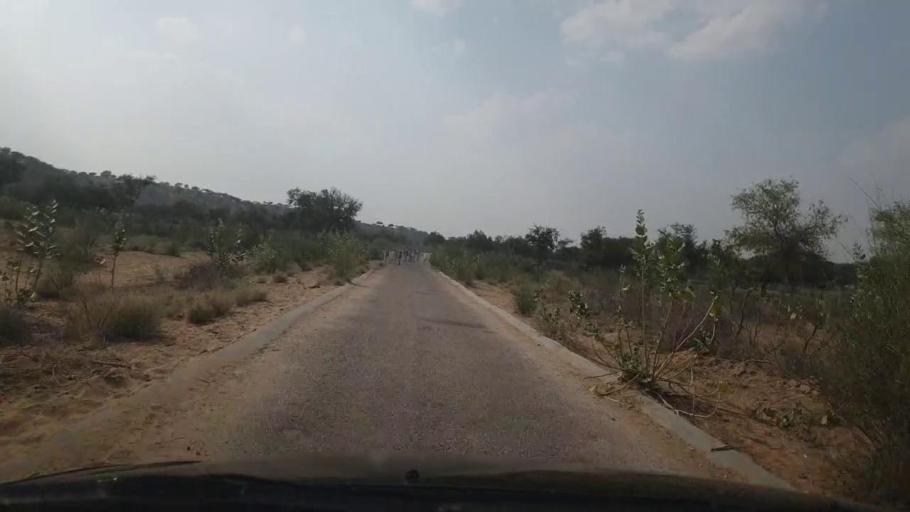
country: PK
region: Sindh
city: Islamkot
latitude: 24.9636
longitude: 70.6111
